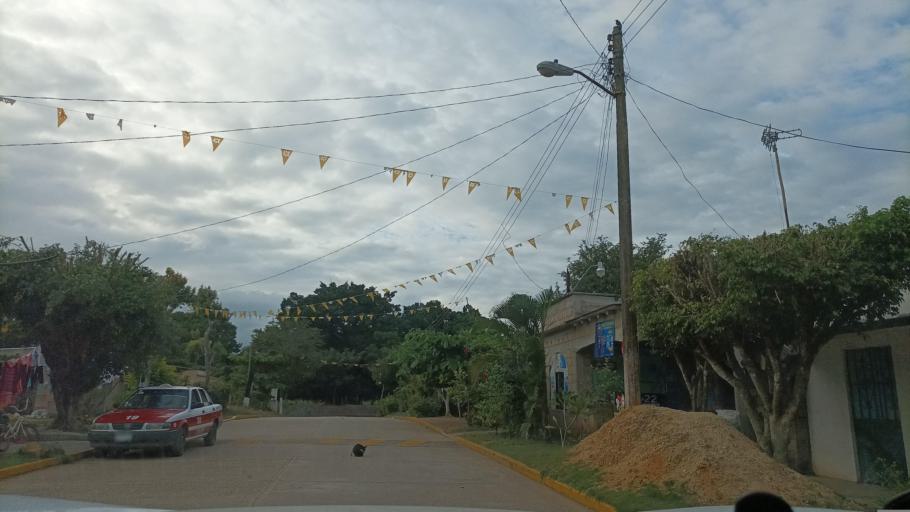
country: MX
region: Veracruz
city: Oluta
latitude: 17.8940
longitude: -94.8703
